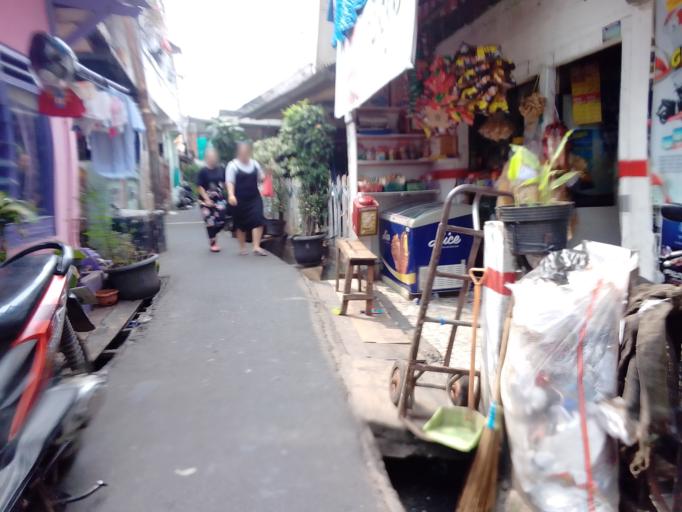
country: ID
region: Jakarta Raya
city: Jakarta
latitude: -6.1898
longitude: 106.8082
